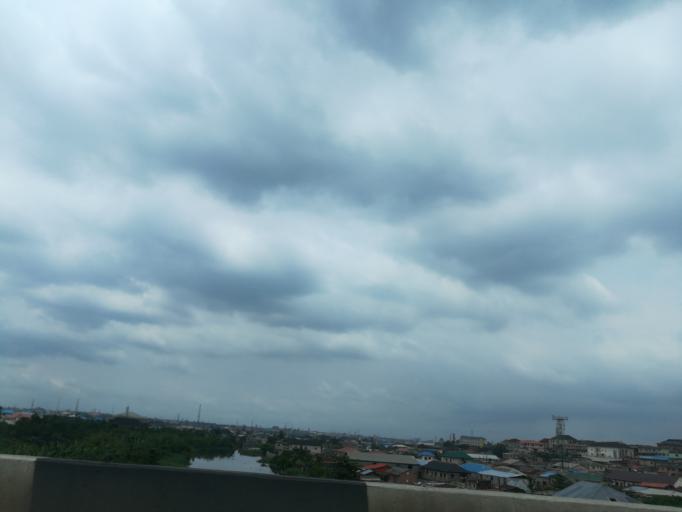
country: NG
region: Lagos
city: Ojota
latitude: 6.5674
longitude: 3.3963
